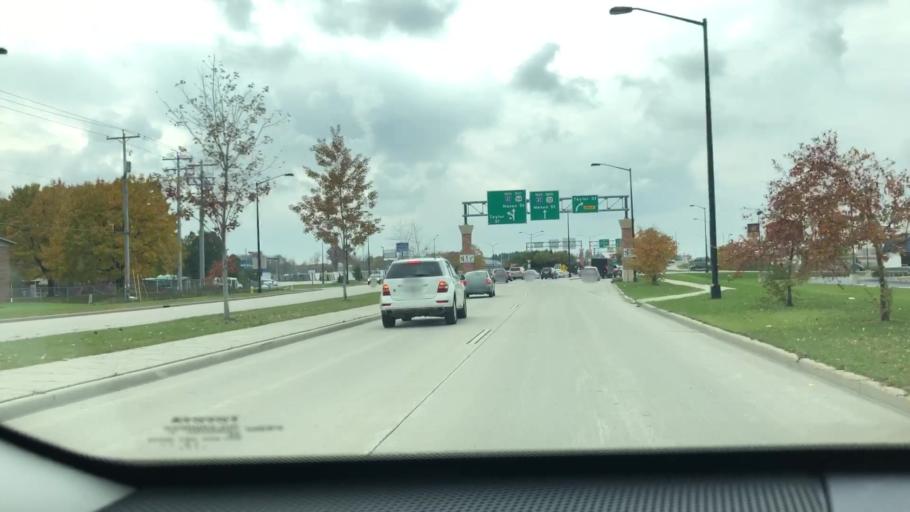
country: US
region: Wisconsin
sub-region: Brown County
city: Howard
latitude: 44.5244
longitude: -88.0772
